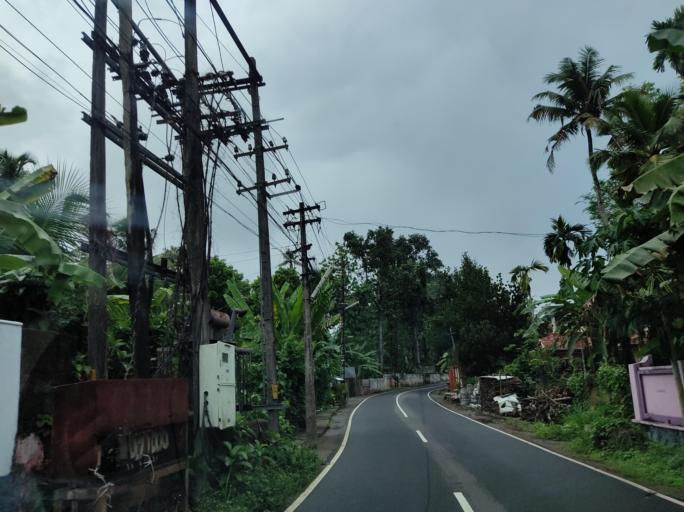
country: IN
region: Kerala
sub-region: Alappuzha
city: Mavelikara
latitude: 9.2390
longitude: 76.5534
